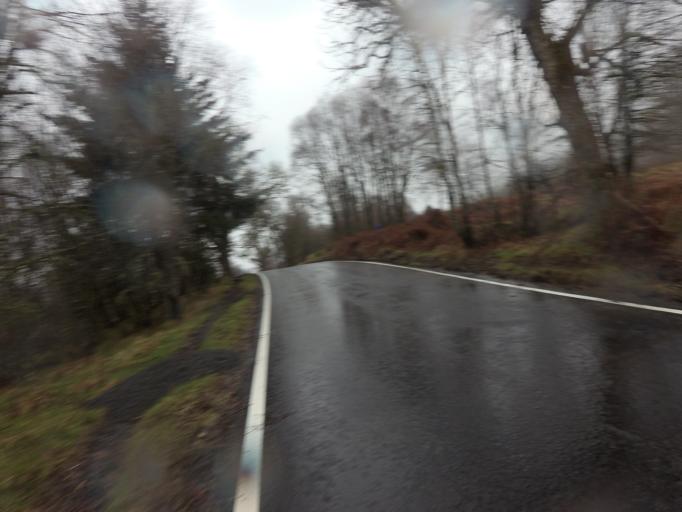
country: GB
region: Scotland
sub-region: West Dunbartonshire
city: Balloch
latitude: 56.1960
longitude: -4.5195
